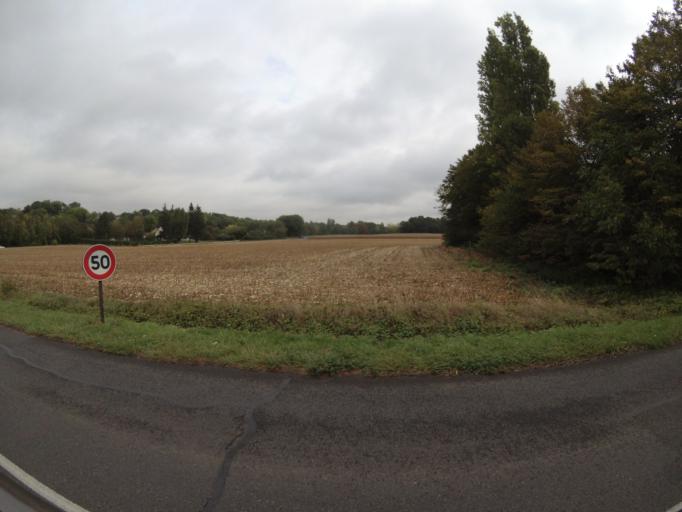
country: FR
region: Ile-de-France
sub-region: Departement de Seine-et-Marne
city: Guermantes
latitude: 48.8590
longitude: 2.7035
